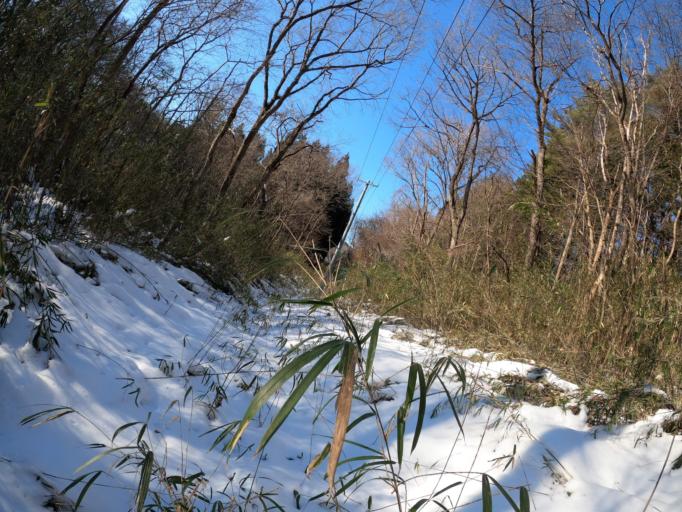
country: JP
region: Iwate
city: Ichinoseki
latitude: 38.9043
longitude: 141.1215
